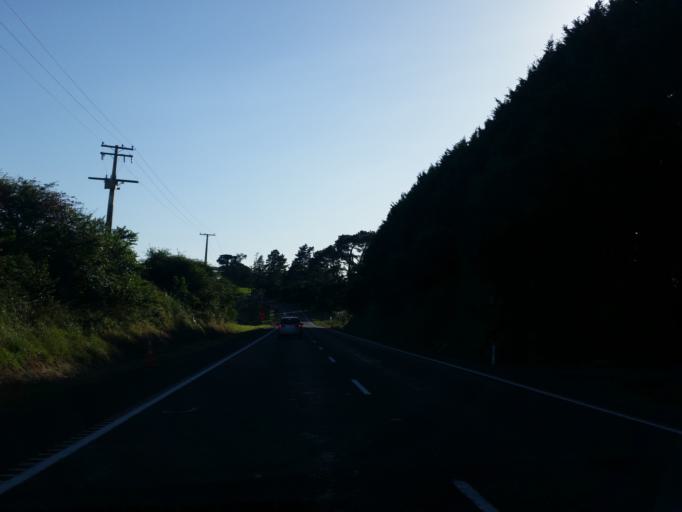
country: NZ
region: Bay of Plenty
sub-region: Western Bay of Plenty District
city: Waihi Beach
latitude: -37.4676
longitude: 175.9363
